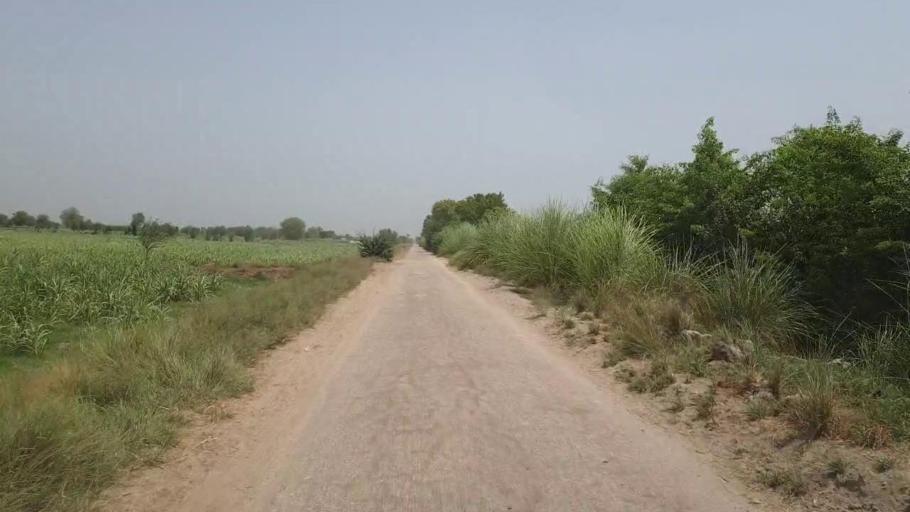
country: PK
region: Sindh
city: Nawabshah
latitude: 26.2961
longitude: 68.3066
